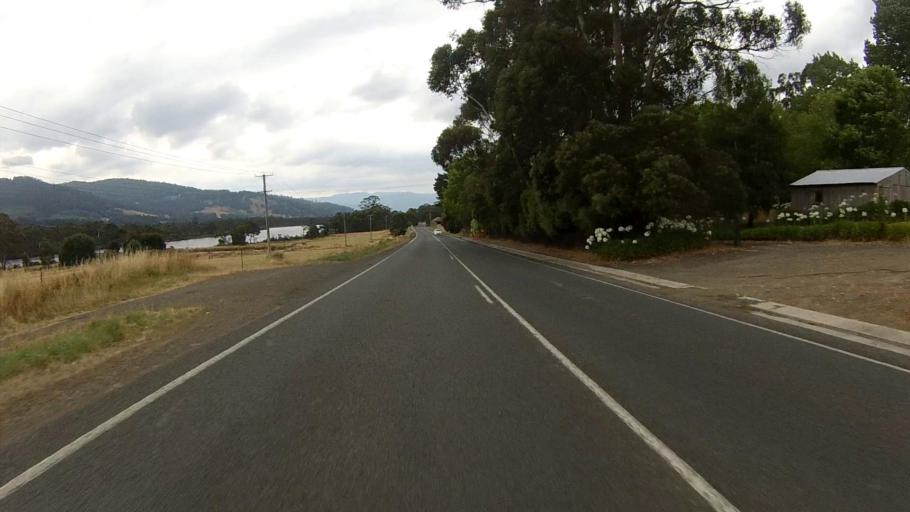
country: AU
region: Tasmania
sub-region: Huon Valley
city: Franklin
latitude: -43.0857
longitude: 147.0296
